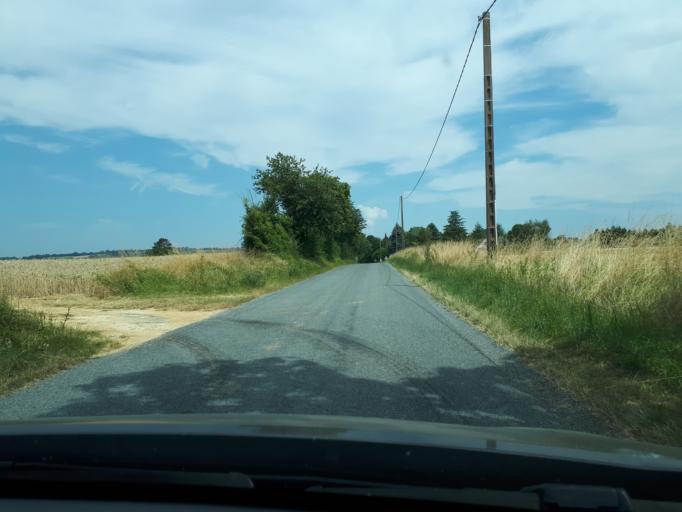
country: FR
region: Centre
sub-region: Departement du Cher
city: Sancerre
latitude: 47.2828
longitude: 2.7527
